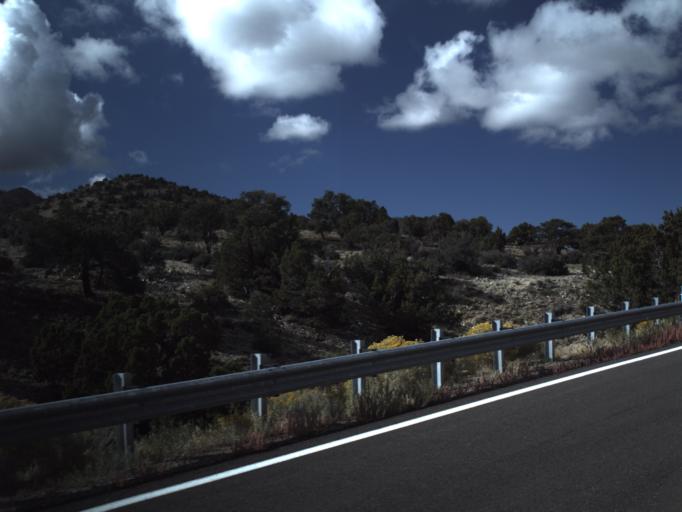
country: US
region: Utah
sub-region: Beaver County
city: Milford
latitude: 38.5172
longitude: -113.5430
